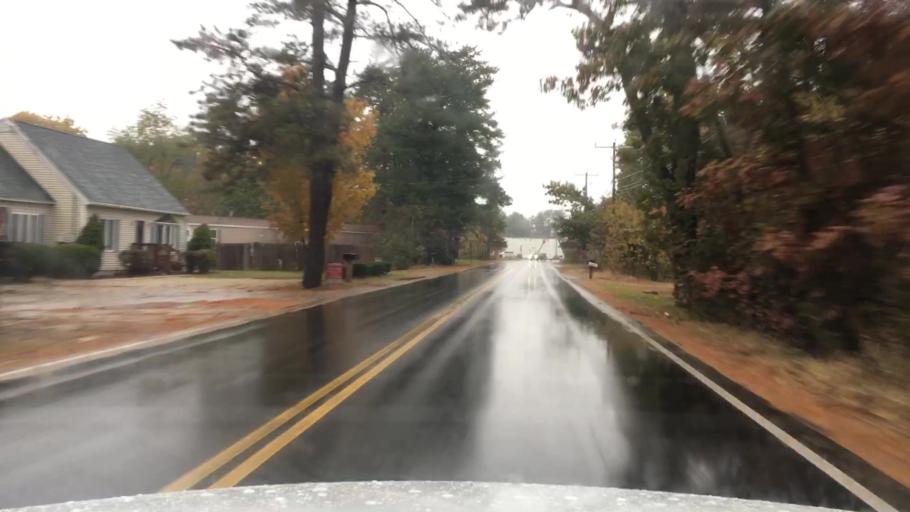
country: US
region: New Hampshire
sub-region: Strafford County
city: Rochester
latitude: 43.3449
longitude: -70.9724
